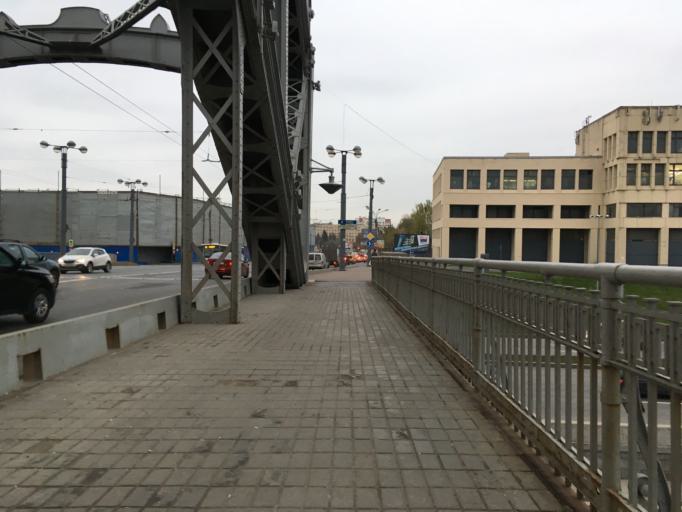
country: RU
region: St.-Petersburg
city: Centralniy
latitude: 59.9425
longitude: 30.4037
